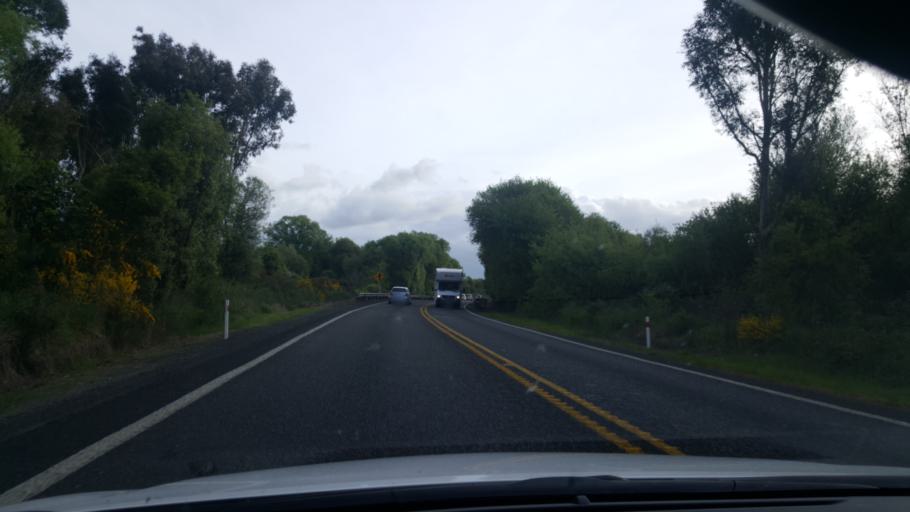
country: NZ
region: Waikato
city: Turangi
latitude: -38.9465
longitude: 175.8506
